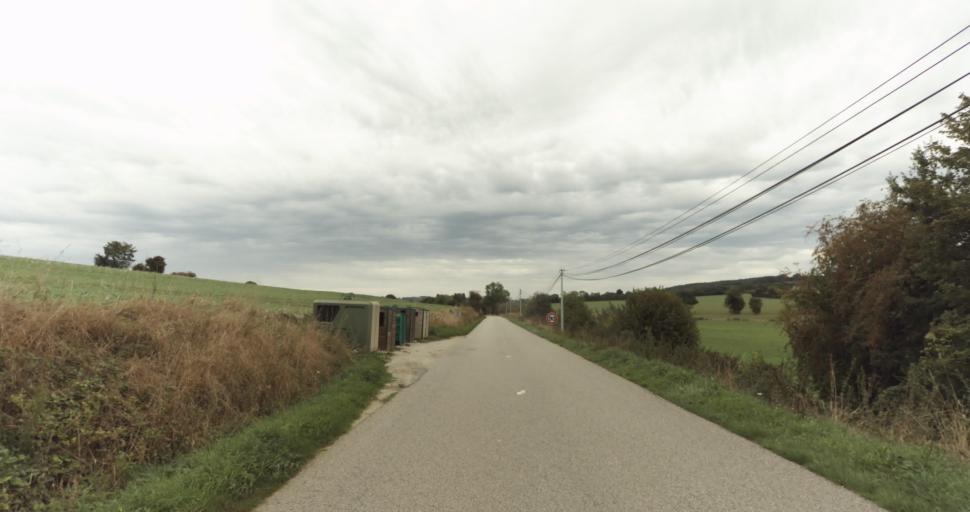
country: FR
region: Lower Normandy
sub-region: Departement de l'Orne
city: Gace
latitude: 48.6952
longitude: 0.2755
